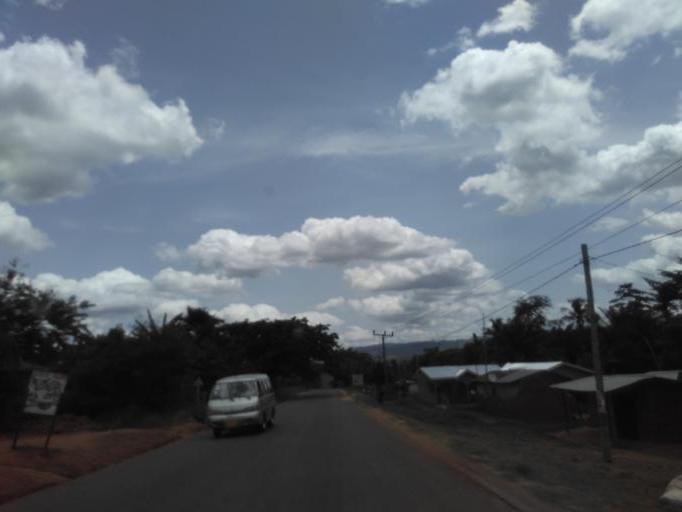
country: GH
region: Eastern
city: Koforidua
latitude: 6.1207
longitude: -0.1524
